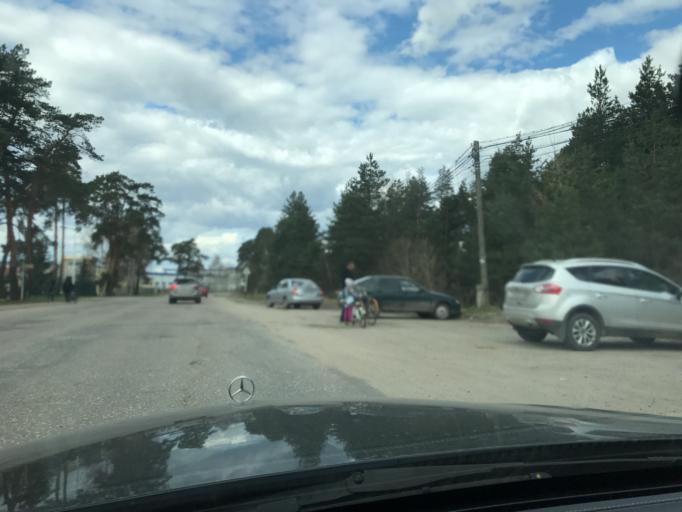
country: RU
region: Vladimir
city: Pokrov
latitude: 55.9023
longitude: 39.1941
